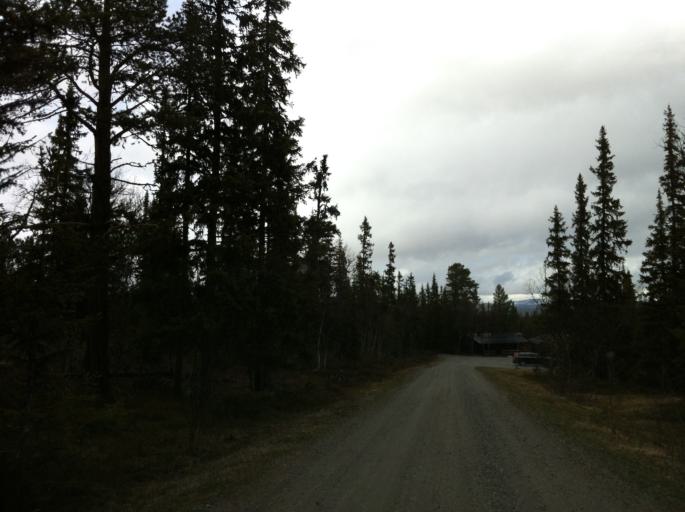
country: NO
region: Hedmark
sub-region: Engerdal
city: Engerdal
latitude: 62.5402
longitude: 12.4459
